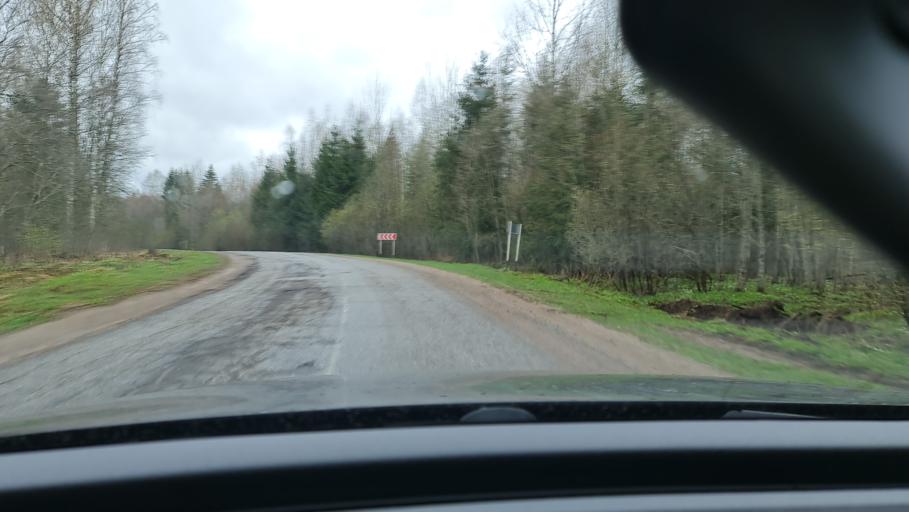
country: RU
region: Novgorod
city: Marevo
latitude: 57.2613
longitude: 32.0685
